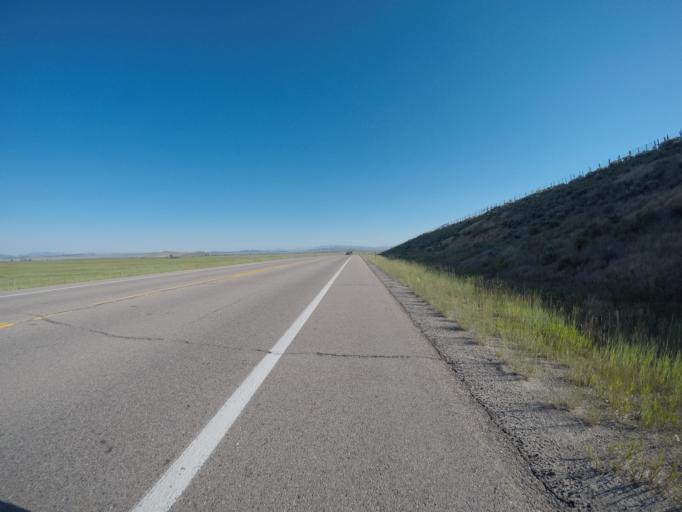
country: US
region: Wyoming
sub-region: Sublette County
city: Pinedale
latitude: 42.9446
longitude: -110.0840
